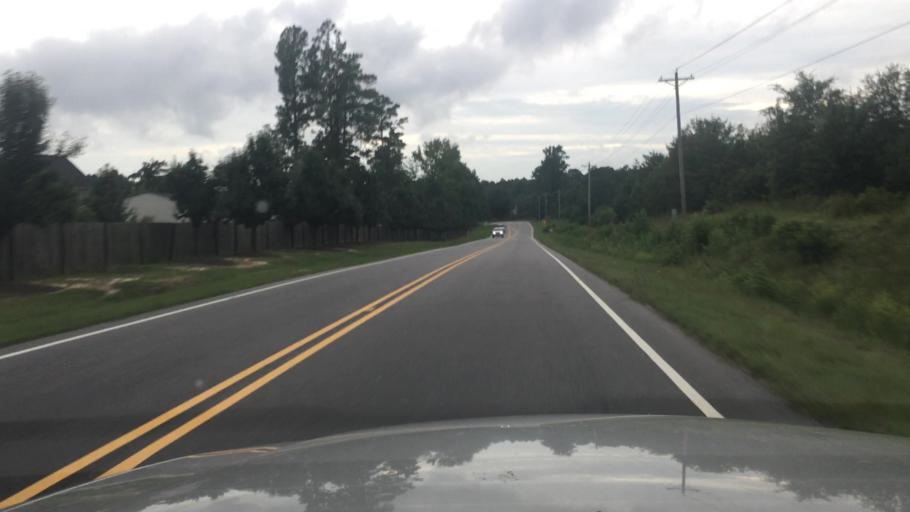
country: US
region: North Carolina
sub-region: Hoke County
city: Rockfish
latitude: 34.9613
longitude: -79.0317
